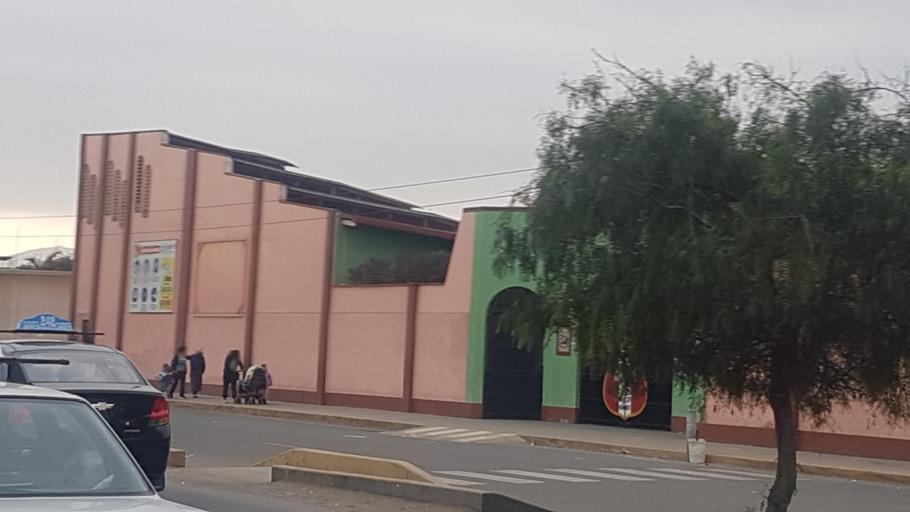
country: PE
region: Ancash
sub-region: Provincia de Santa
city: Chimbote
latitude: -9.0922
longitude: -78.5703
